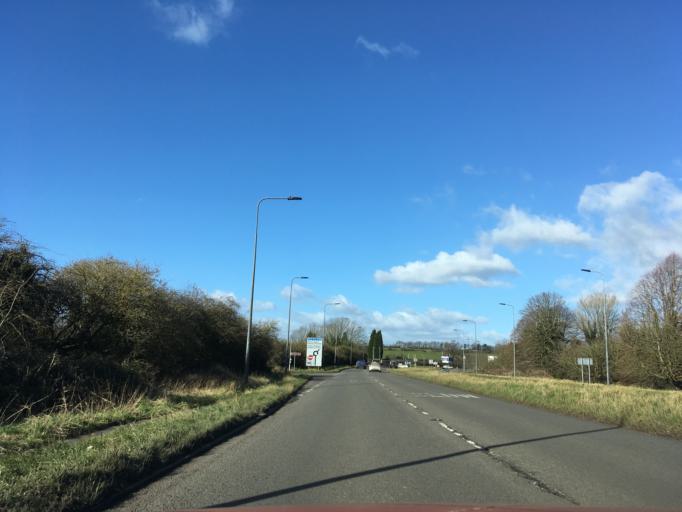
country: GB
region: England
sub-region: South Gloucestershire
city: Severn Beach
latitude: 51.5163
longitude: -2.6216
